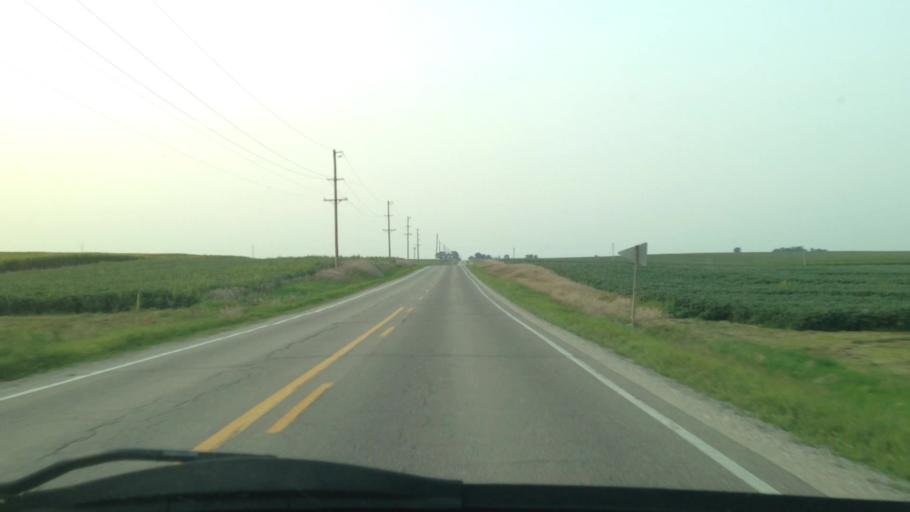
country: US
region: Iowa
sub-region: Iowa County
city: Marengo
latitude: 41.9460
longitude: -92.0851
